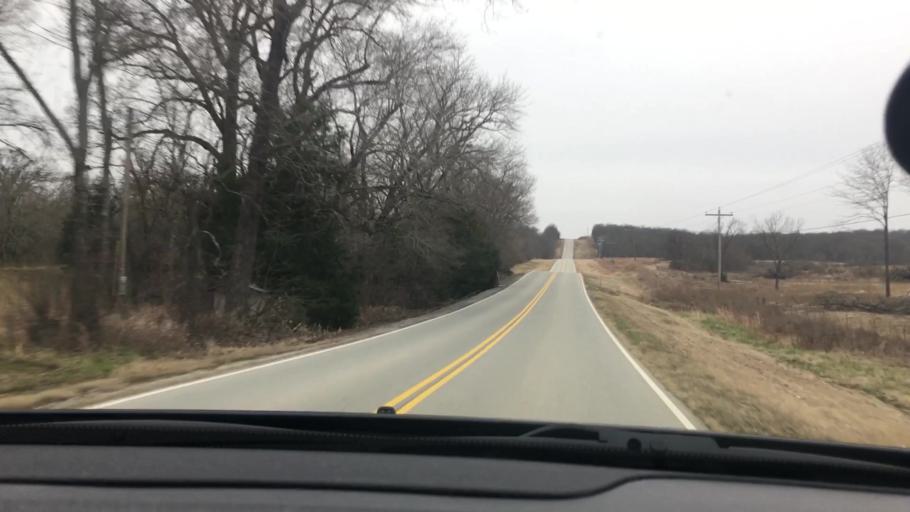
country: US
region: Oklahoma
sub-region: Coal County
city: Coalgate
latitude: 34.5057
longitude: -96.3095
